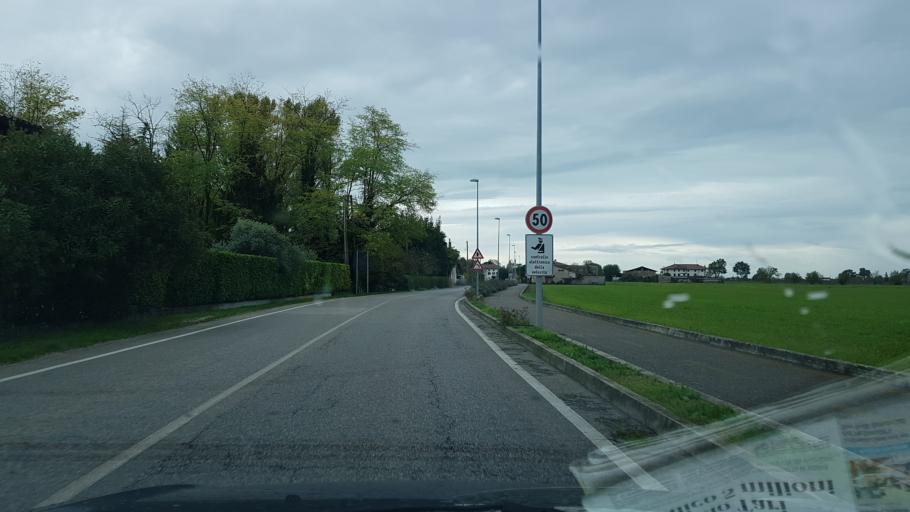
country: IT
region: Friuli Venezia Giulia
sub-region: Provincia di Udine
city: Villa Vicentina
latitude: 45.8056
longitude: 13.4003
